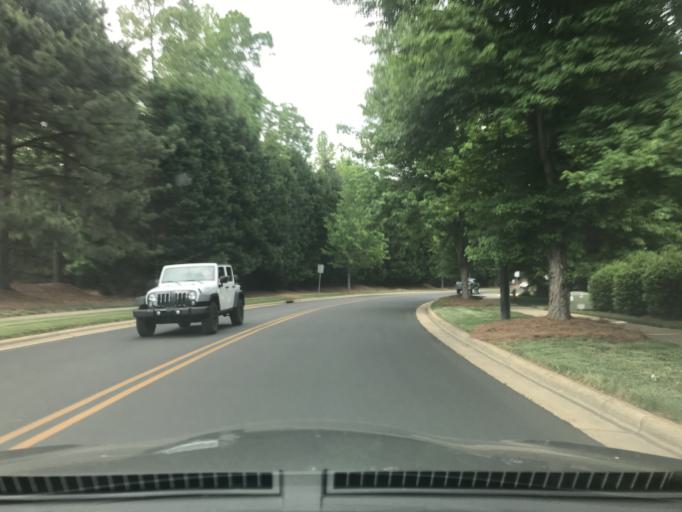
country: US
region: North Carolina
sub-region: Wake County
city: Wake Forest
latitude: 35.9112
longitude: -78.5873
